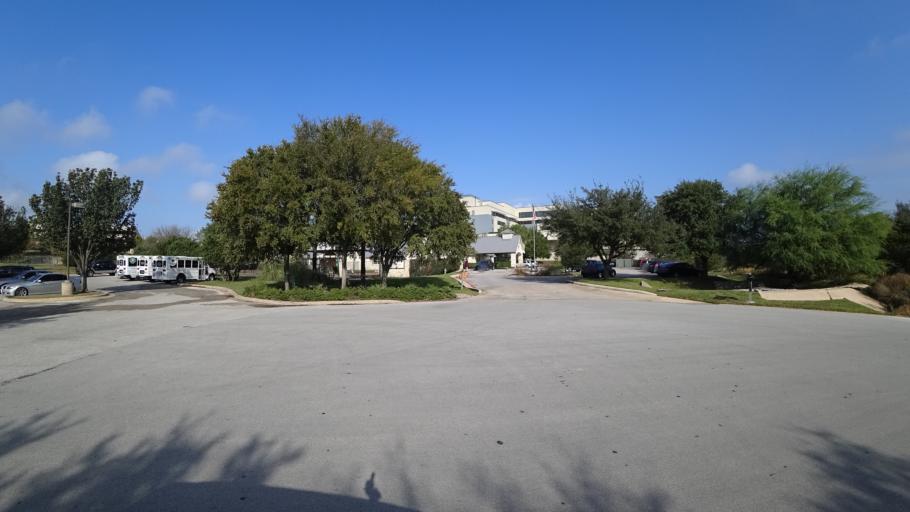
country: US
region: Texas
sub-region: Travis County
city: Bee Cave
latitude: 30.3082
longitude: -97.9352
